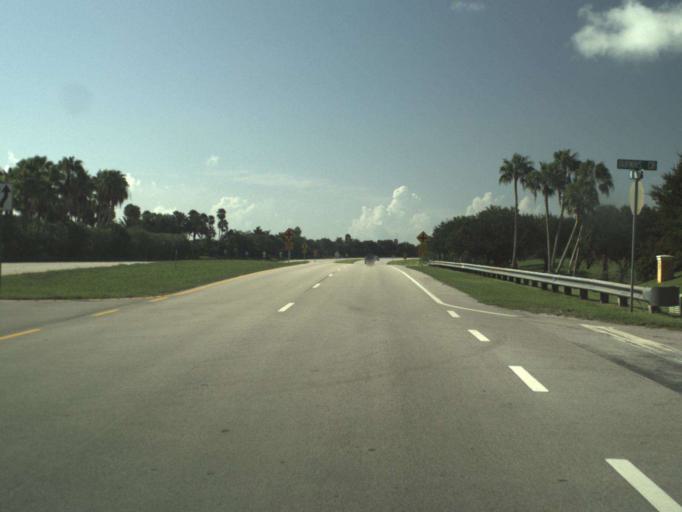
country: US
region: Florida
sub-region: Indian River County
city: Gifford
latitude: 27.6853
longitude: -80.4067
